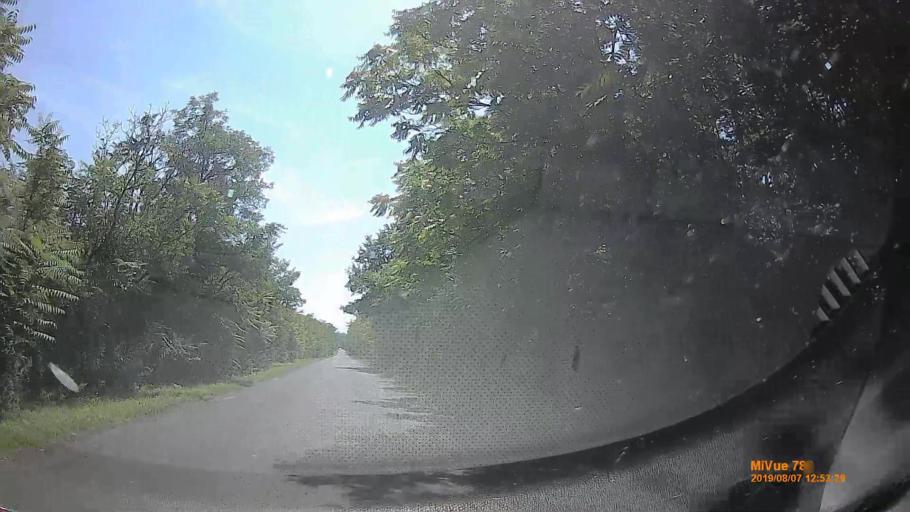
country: HU
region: Zala
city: Cserszegtomaj
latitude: 46.8355
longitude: 17.2694
